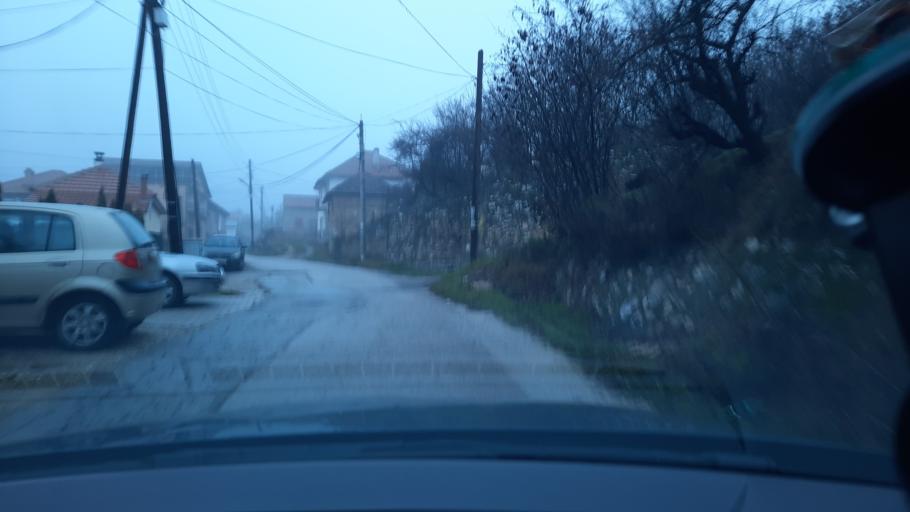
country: MK
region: Vrapciste
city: Vrapciste
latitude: 41.8390
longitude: 20.8809
